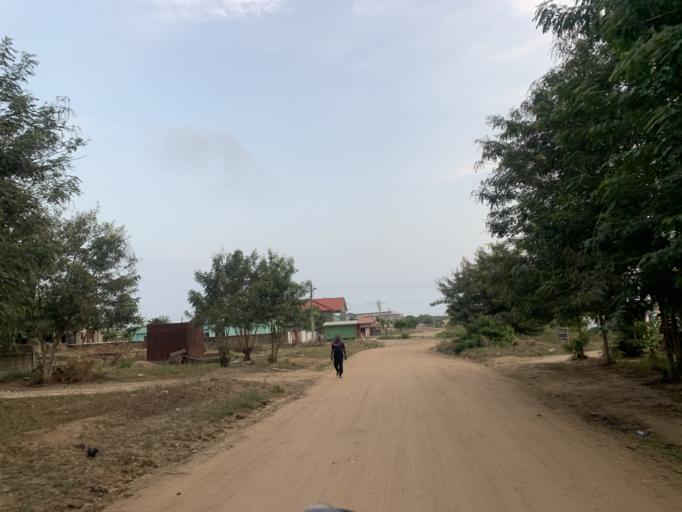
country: GH
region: Central
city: Winneba
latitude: 5.3780
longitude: -0.6334
